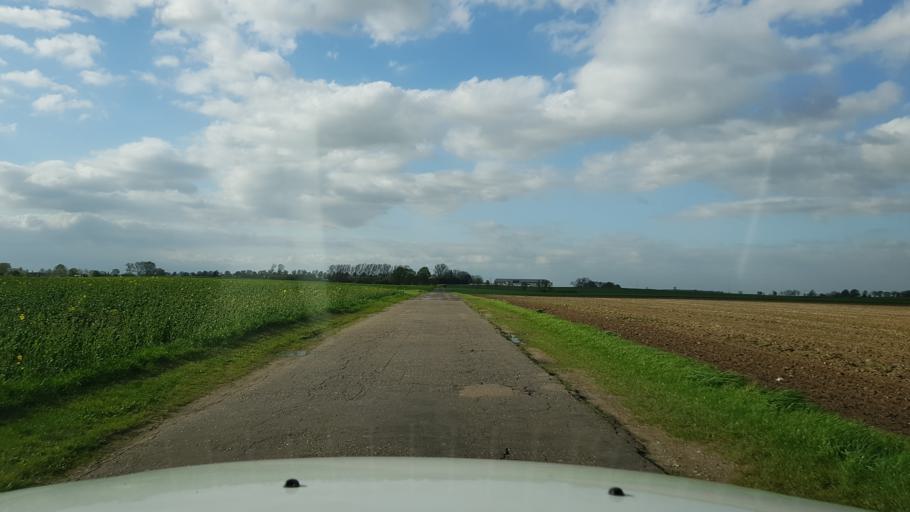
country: PL
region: West Pomeranian Voivodeship
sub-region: Powiat pyrzycki
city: Przelewice
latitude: 53.0649
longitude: 15.1048
